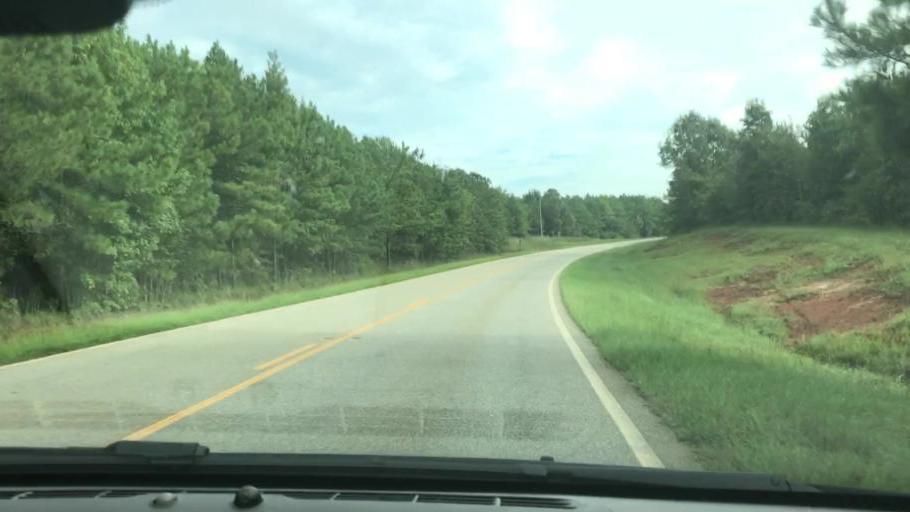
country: US
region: Georgia
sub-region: Stewart County
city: Lumpkin
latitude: 32.0144
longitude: -84.9311
